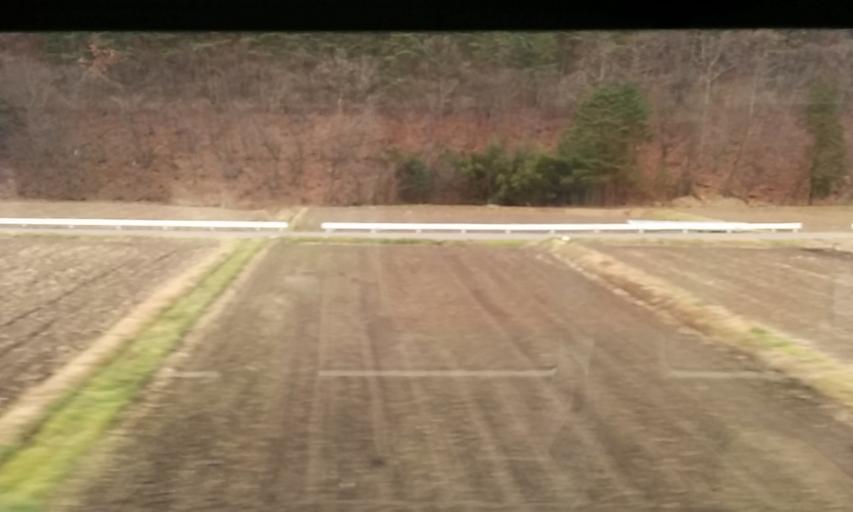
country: JP
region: Nagano
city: Ueda
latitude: 36.4546
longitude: 138.0777
